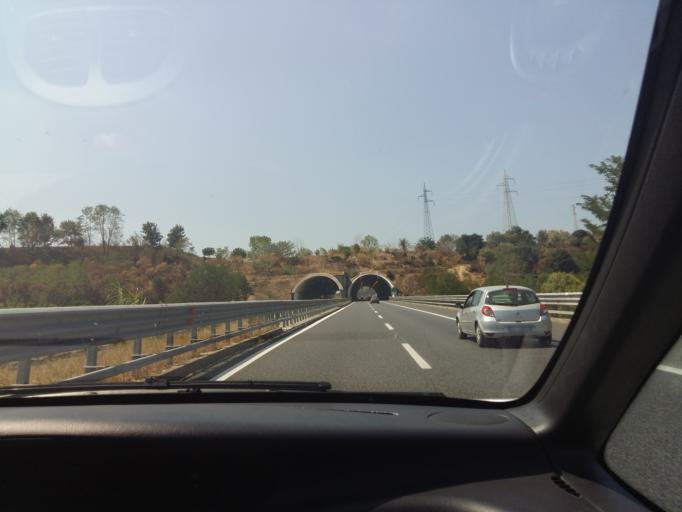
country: IT
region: Calabria
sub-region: Provincia di Reggio Calabria
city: Rosarno
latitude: 38.4703
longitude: 15.9934
